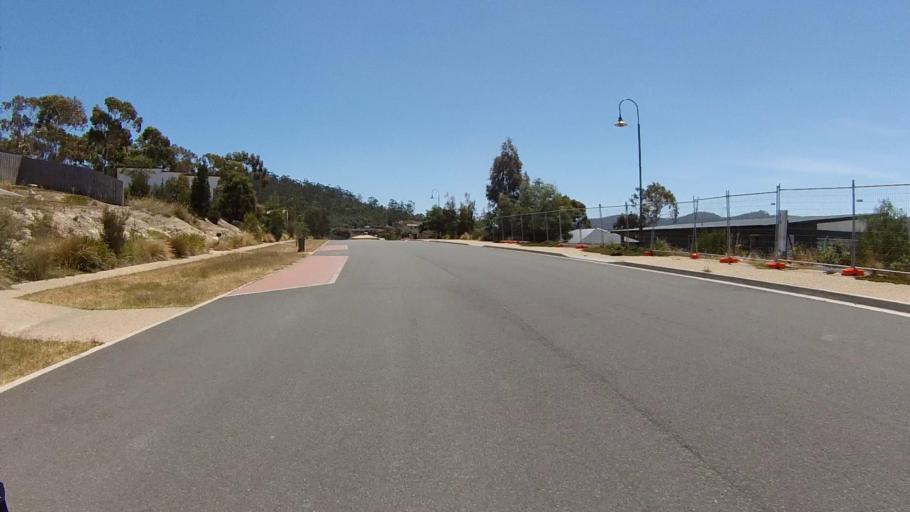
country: AU
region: Tasmania
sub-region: Clarence
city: Rokeby
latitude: -42.9069
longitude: 147.4289
